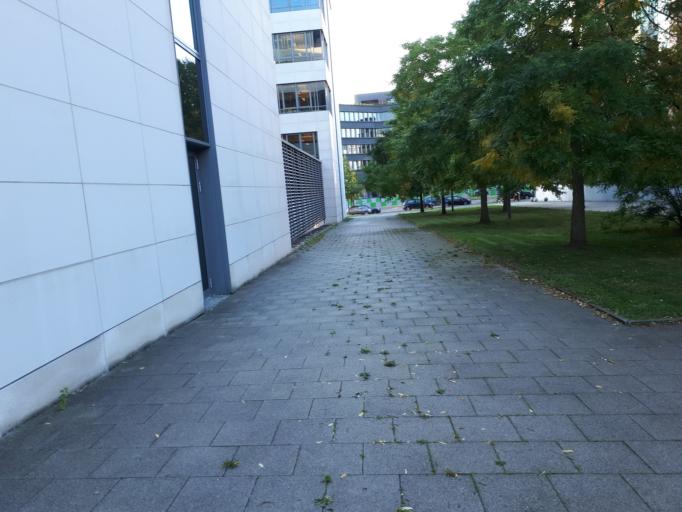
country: LU
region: Luxembourg
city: Kirchberg
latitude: 49.6303
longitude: 6.1699
